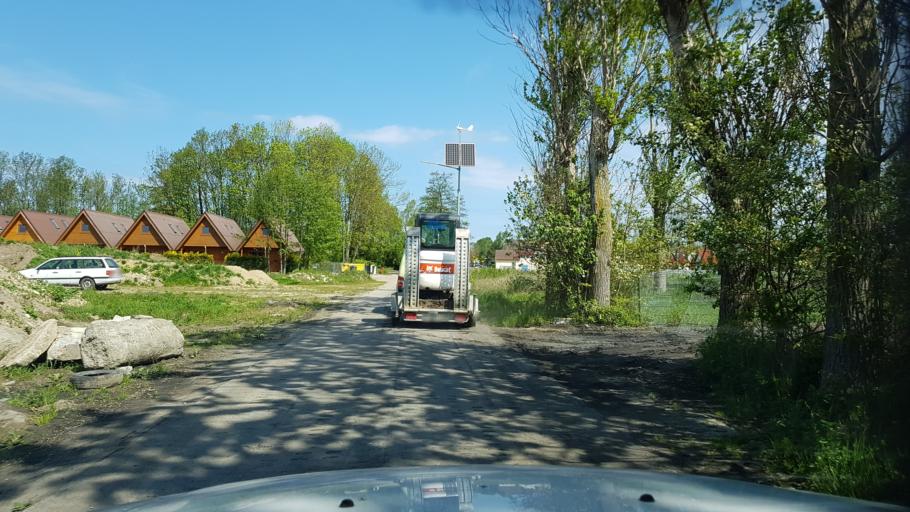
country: PL
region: West Pomeranian Voivodeship
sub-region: Powiat koszalinski
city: Mielno
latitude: 54.2439
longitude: 15.9559
